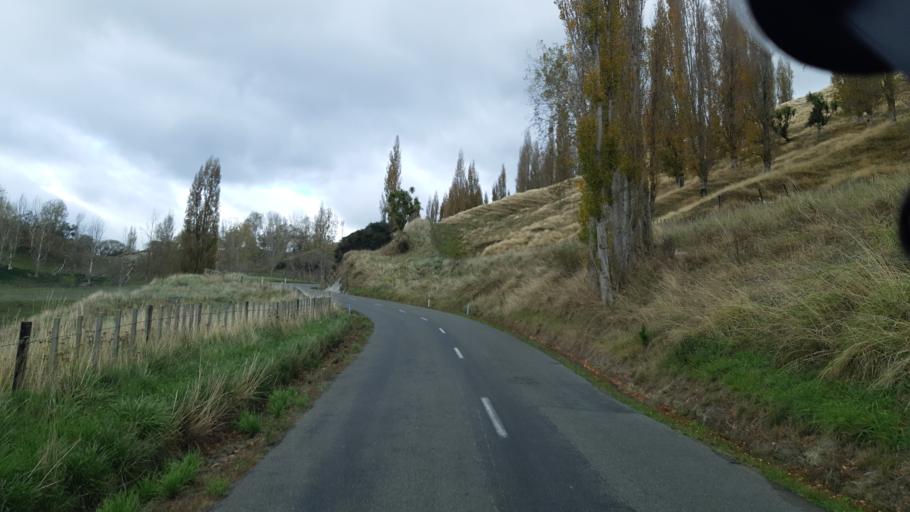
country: NZ
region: Manawatu-Wanganui
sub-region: Ruapehu District
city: Waiouru
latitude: -39.6519
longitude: 175.7293
